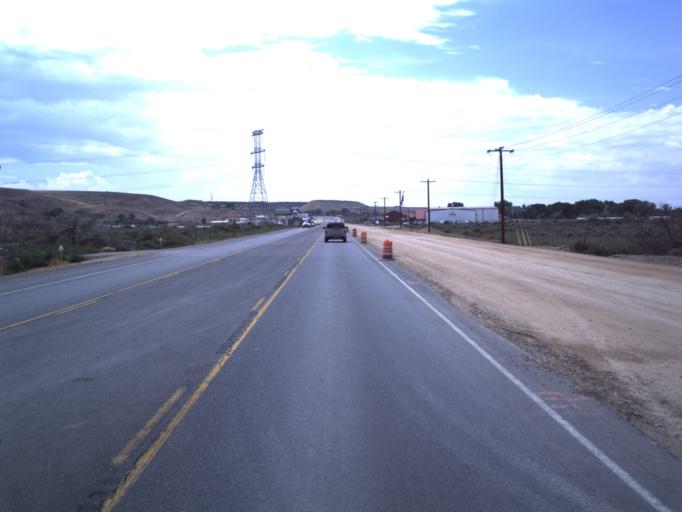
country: US
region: Utah
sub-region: Duchesne County
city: Roosevelt
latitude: 40.2646
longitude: -110.0477
